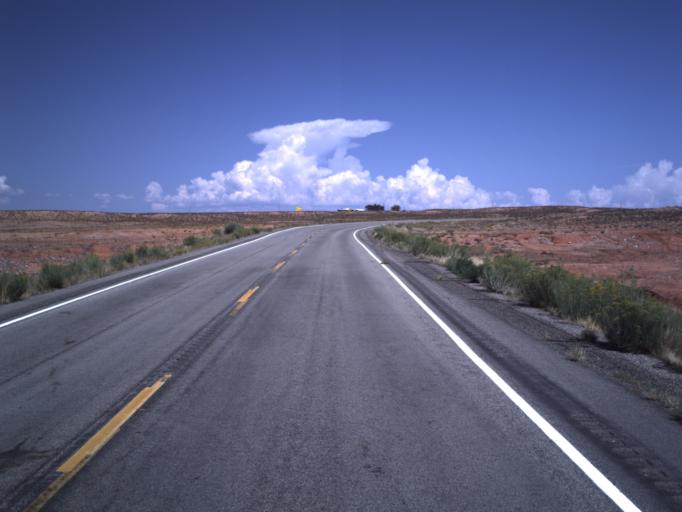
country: US
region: Utah
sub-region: San Juan County
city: Blanding
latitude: 37.0104
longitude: -109.6121
